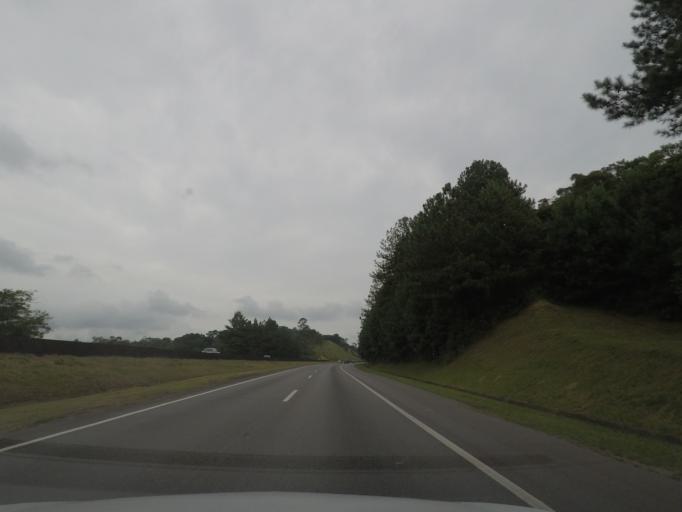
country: BR
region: Sao Paulo
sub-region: Juquitiba
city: Juquitiba
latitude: -23.9624
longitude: -47.1224
